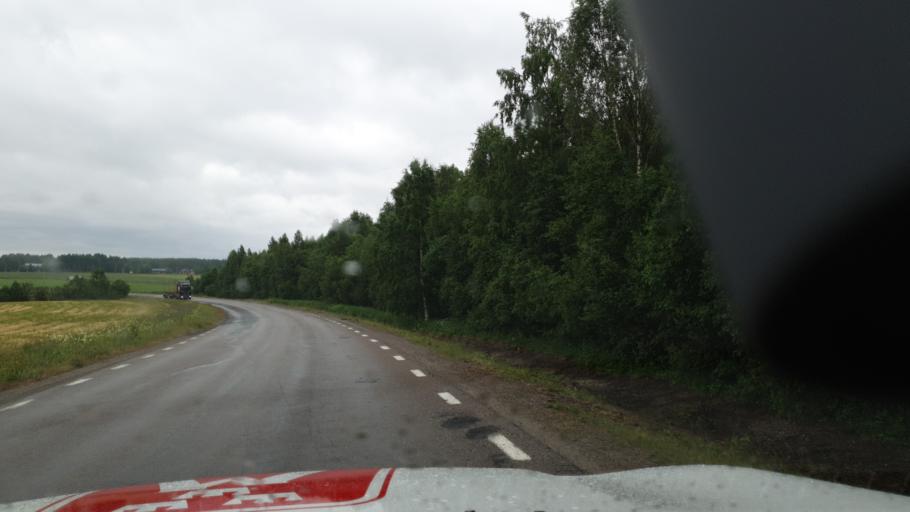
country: SE
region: Vaesterbotten
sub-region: Vannas Kommun
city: Vannasby
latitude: 63.7785
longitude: 19.8478
